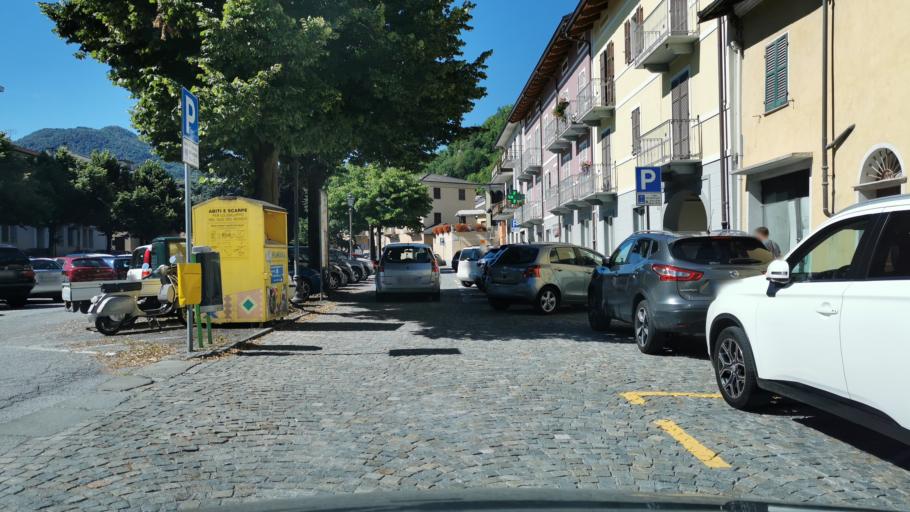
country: IT
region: Piedmont
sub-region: Provincia di Cuneo
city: Boves
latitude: 44.3303
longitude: 7.5497
